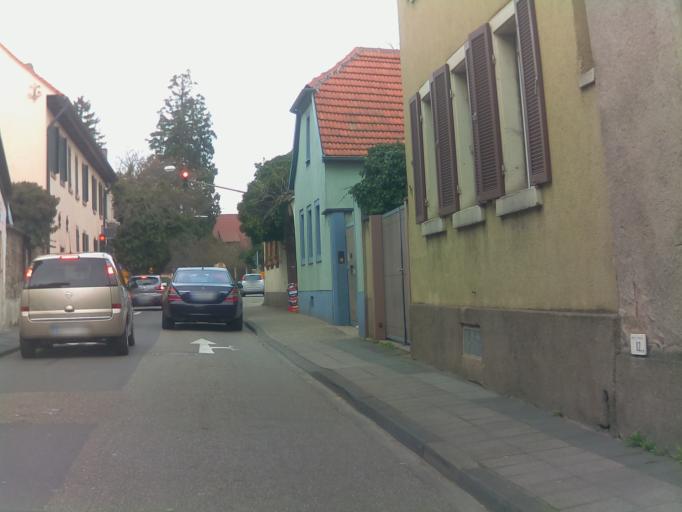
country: DE
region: Rheinland-Pfalz
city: Ruppertsberg
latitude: 49.3687
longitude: 8.1741
